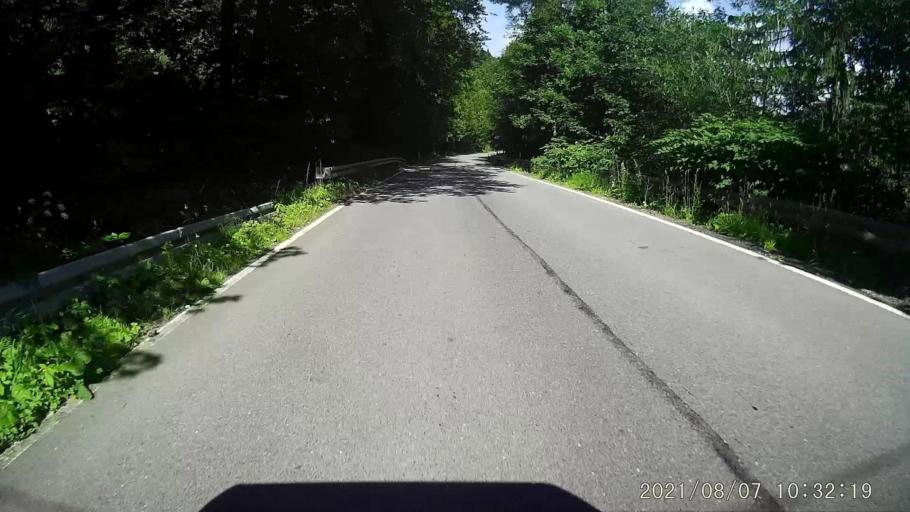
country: PL
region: Lower Silesian Voivodeship
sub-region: Powiat klodzki
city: Duszniki-Zdroj
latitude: 50.3898
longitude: 16.3569
